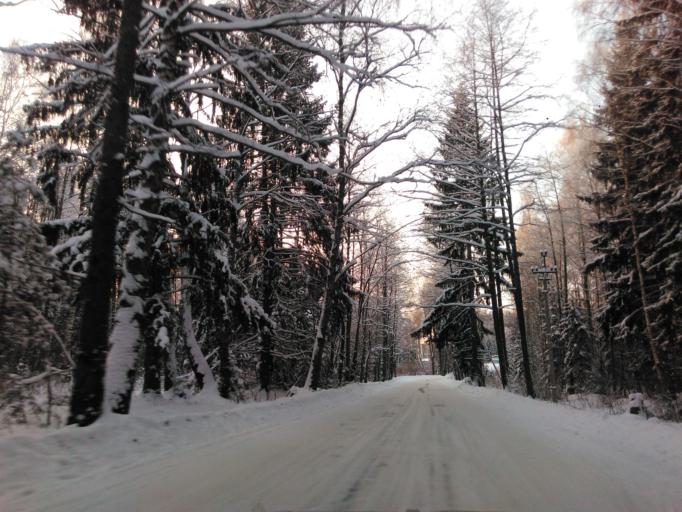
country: RU
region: Tverskaya
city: Konakovo
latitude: 56.6676
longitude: 36.6865
